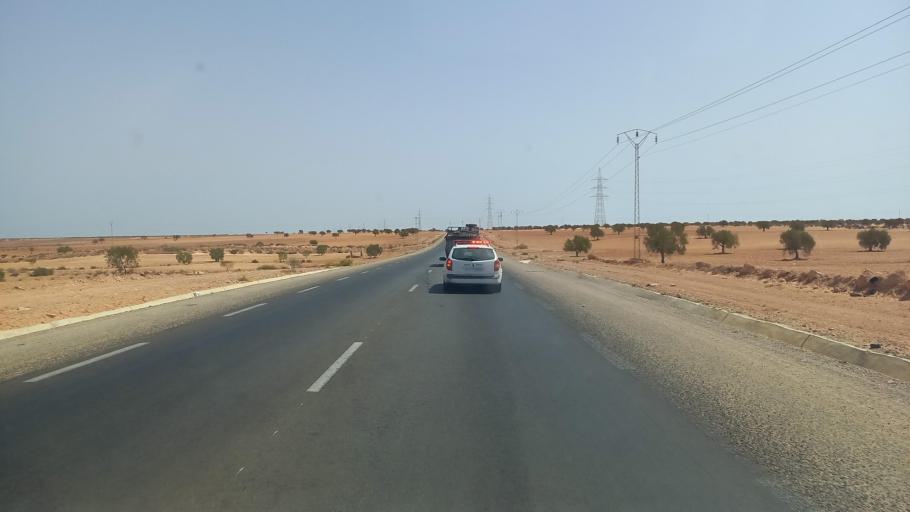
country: TN
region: Madanin
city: Zarzis
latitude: 33.4034
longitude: 10.8498
